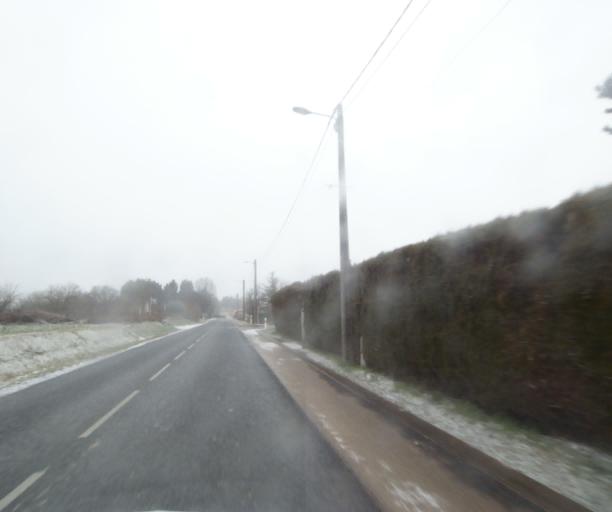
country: FR
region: Champagne-Ardenne
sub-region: Departement de la Haute-Marne
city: Wassy
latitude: 48.5000
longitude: 4.9588
